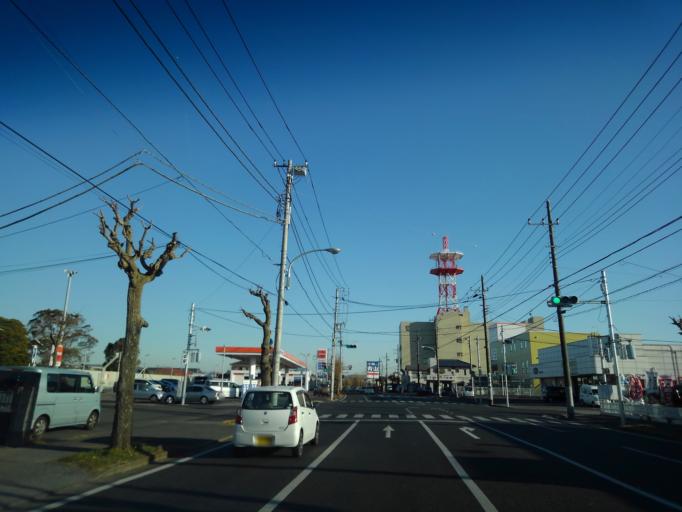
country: JP
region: Chiba
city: Kimitsu
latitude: 35.3274
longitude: 139.9053
